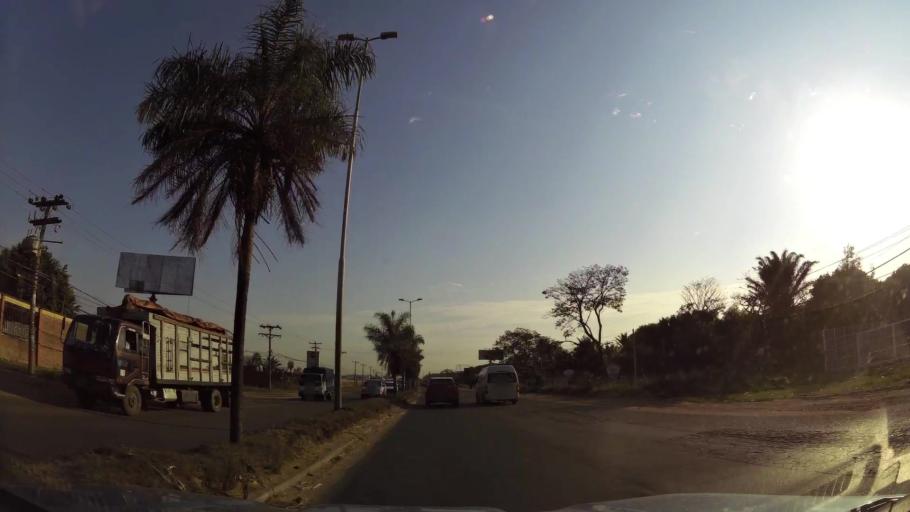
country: BO
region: Santa Cruz
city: Santa Cruz de la Sierra
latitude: -17.7099
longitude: -63.1601
